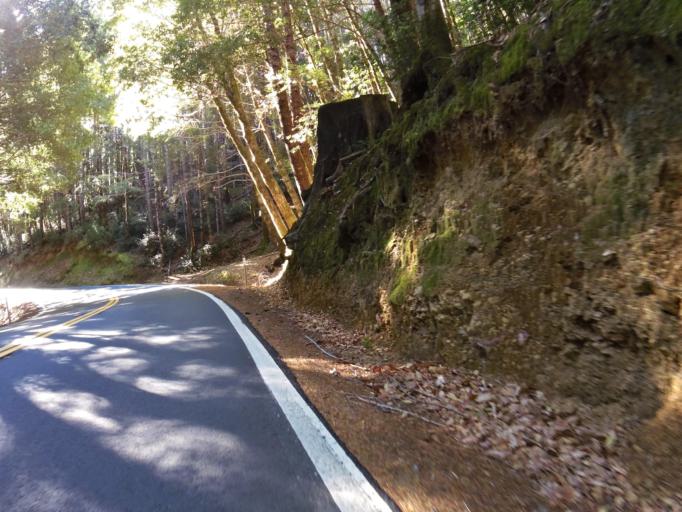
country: US
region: California
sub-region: Humboldt County
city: Redway
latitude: 39.8508
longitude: -123.7355
